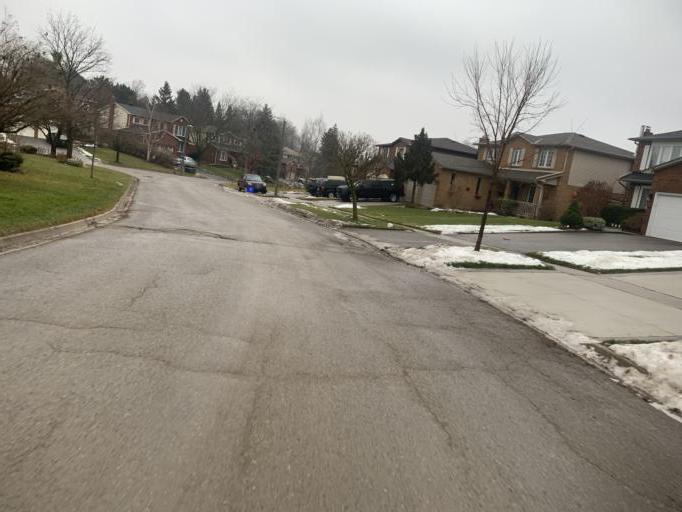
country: CA
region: Ontario
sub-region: Halton
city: Milton
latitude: 43.6597
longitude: -79.9289
